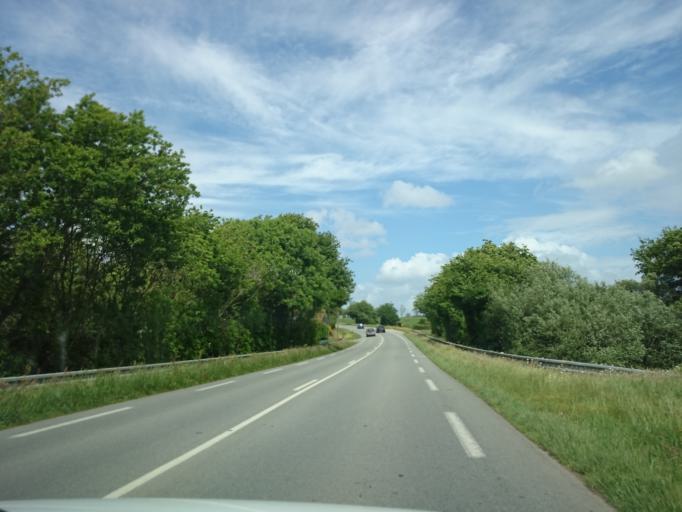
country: FR
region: Brittany
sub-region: Departement du Morbihan
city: Arradon
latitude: 47.6315
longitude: -2.8445
